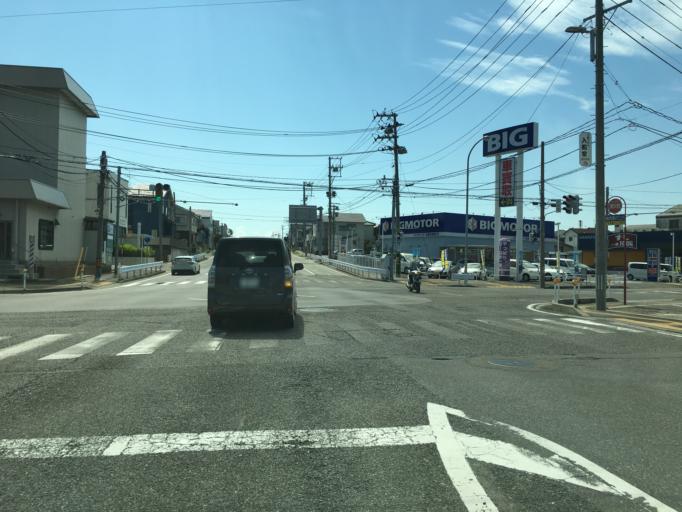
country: JP
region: Niigata
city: Kameda-honcho
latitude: 37.9433
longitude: 139.0868
